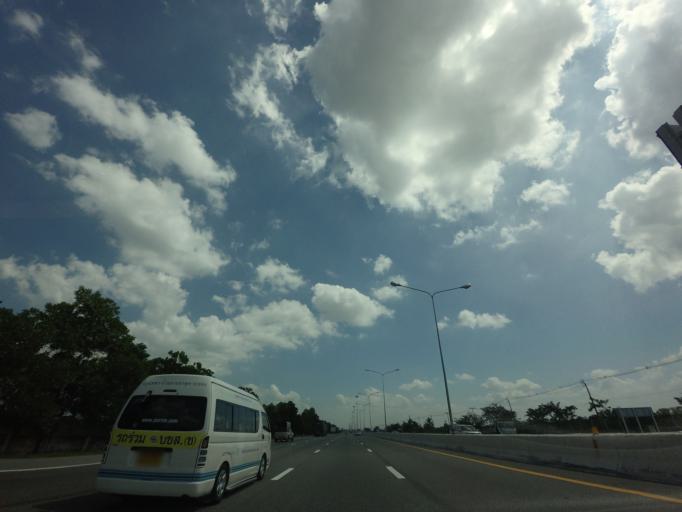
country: TH
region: Samut Prakan
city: Ban Khlong Bang Sao Thong
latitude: 13.6605
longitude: 100.8587
